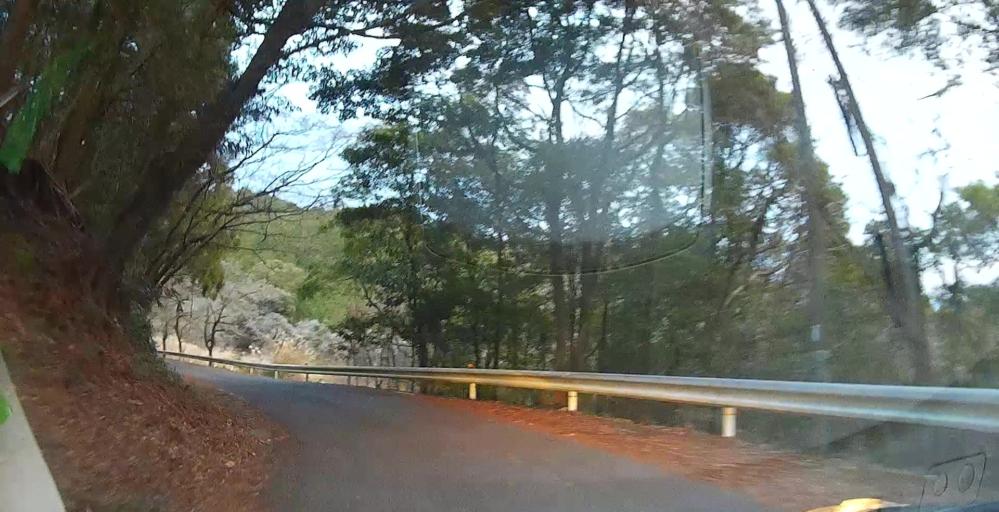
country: JP
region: Kagoshima
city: Izumi
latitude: 32.1212
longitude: 130.4159
